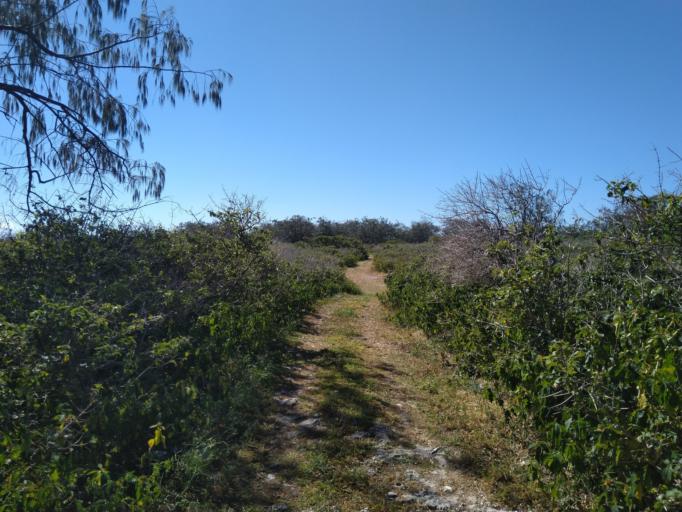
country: AU
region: Queensland
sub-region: Bundaberg
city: Bundaberg
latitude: -24.1118
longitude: 152.7129
